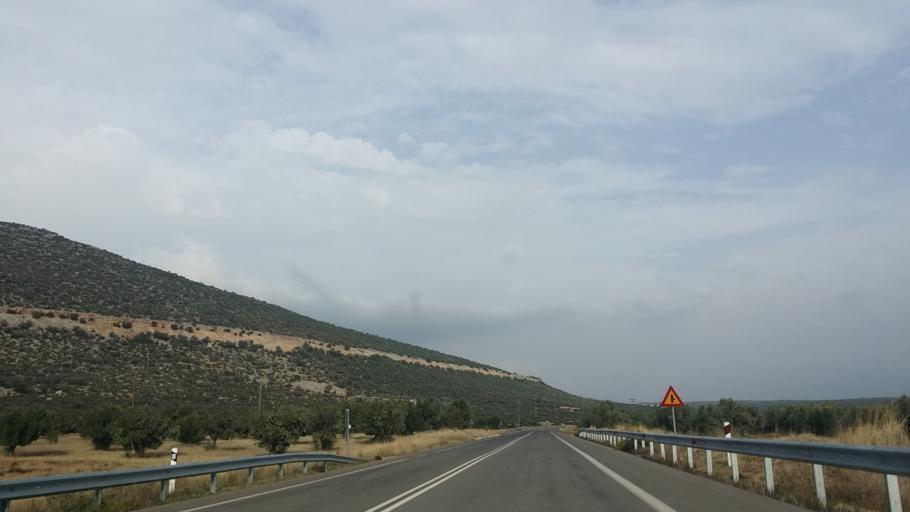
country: GR
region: Central Greece
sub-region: Nomos Voiotias
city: Korini
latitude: 38.2671
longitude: 23.0545
